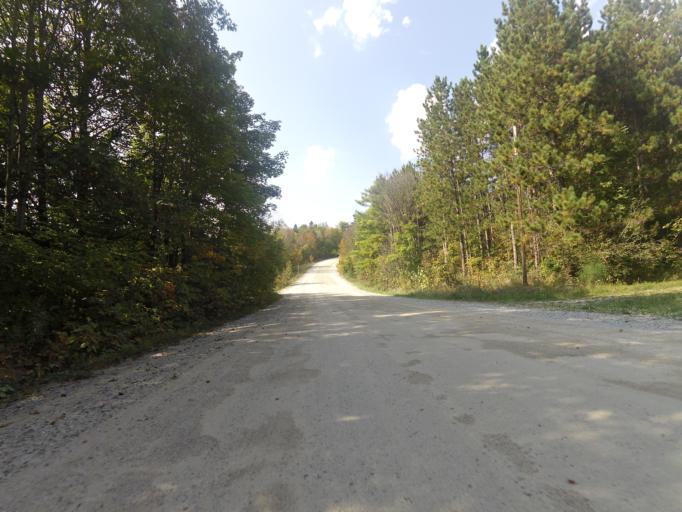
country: CA
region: Ontario
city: Renfrew
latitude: 45.1385
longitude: -76.6669
